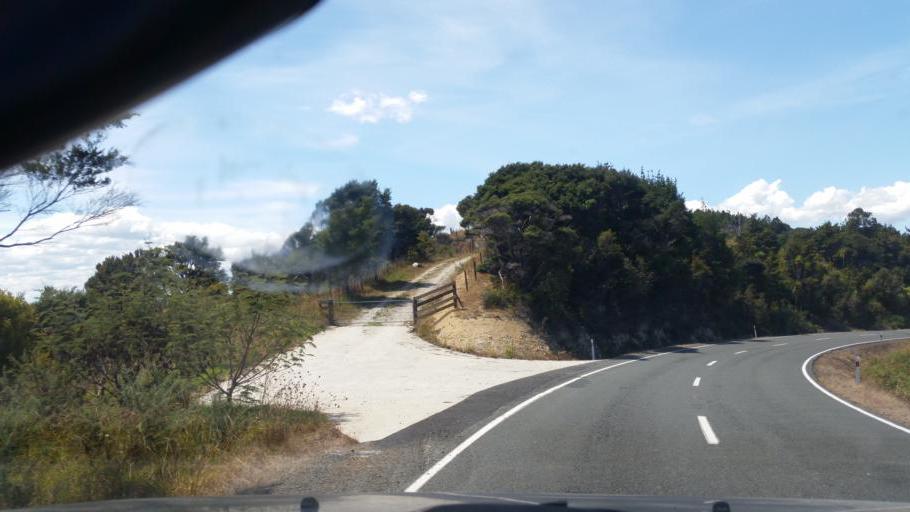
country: NZ
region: Auckland
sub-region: Auckland
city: Wellsford
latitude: -36.1891
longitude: 174.1570
